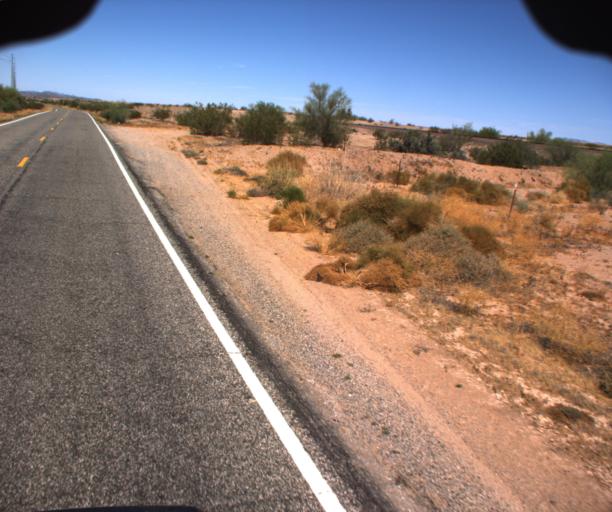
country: US
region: Arizona
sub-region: La Paz County
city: Cienega Springs
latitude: 33.9939
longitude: -114.1344
